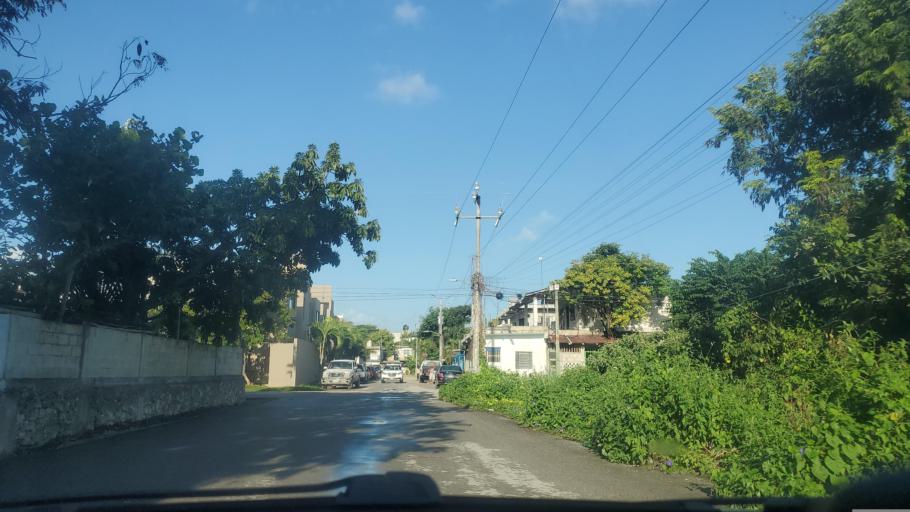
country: MX
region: Quintana Roo
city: Tulum
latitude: 20.2132
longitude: -87.4692
